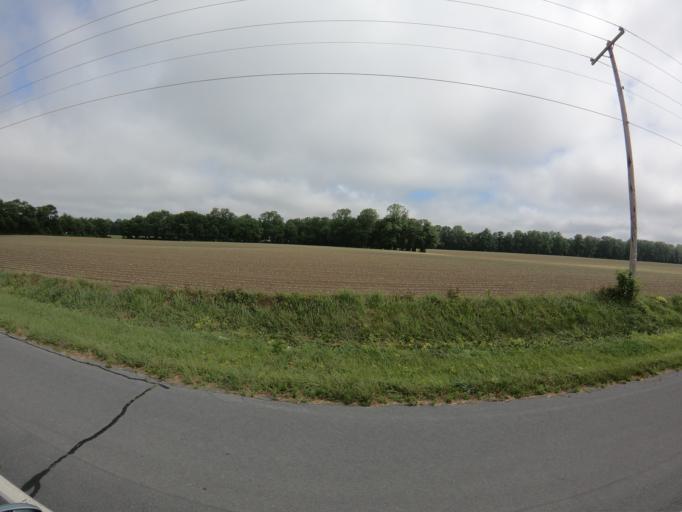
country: US
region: Delaware
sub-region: Kent County
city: Riverview
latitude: 39.0055
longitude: -75.5359
